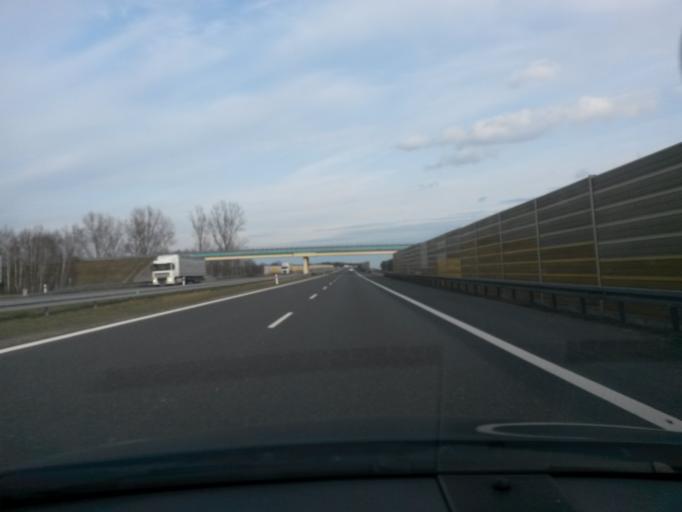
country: PL
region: Lodz Voivodeship
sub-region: Powiat leczycki
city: Swinice Warckie
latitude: 52.0286
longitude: 18.9038
